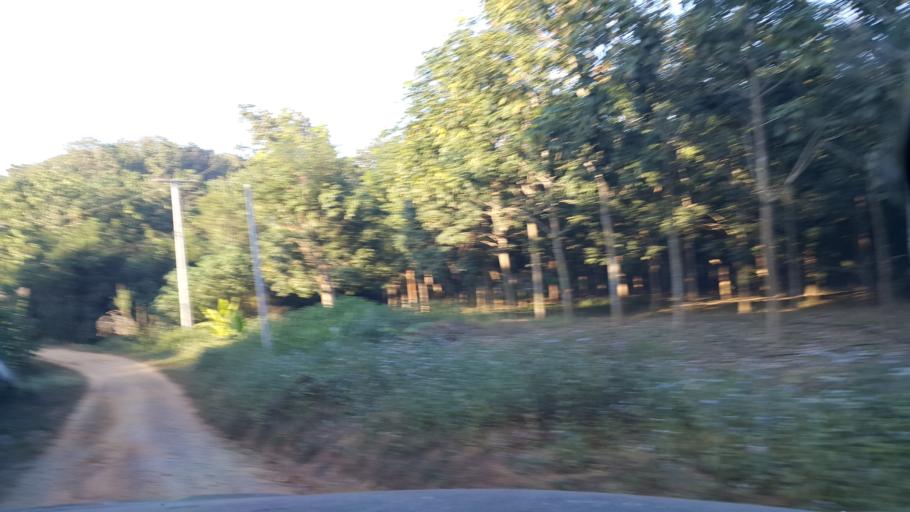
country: TH
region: Sukhothai
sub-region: Amphoe Si Satchanalai
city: Si Satchanalai
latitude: 17.5924
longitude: 99.6173
